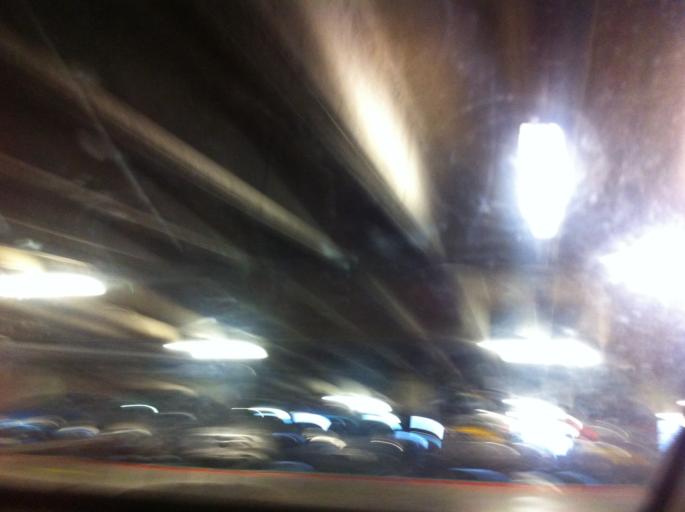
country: GB
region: England
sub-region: Northamptonshire
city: Earls Barton
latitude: 52.2695
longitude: -0.7737
